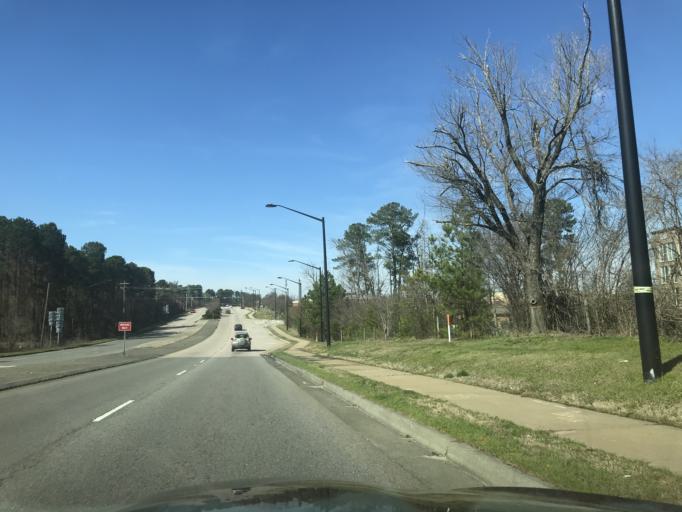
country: US
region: North Carolina
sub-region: Wake County
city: Morrisville
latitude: 35.8630
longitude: -78.8463
